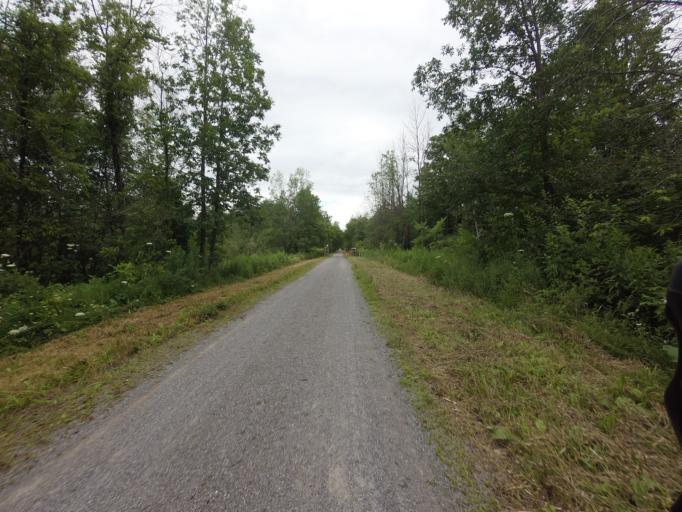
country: CA
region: Ontario
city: Ottawa
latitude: 45.2681
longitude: -75.6238
